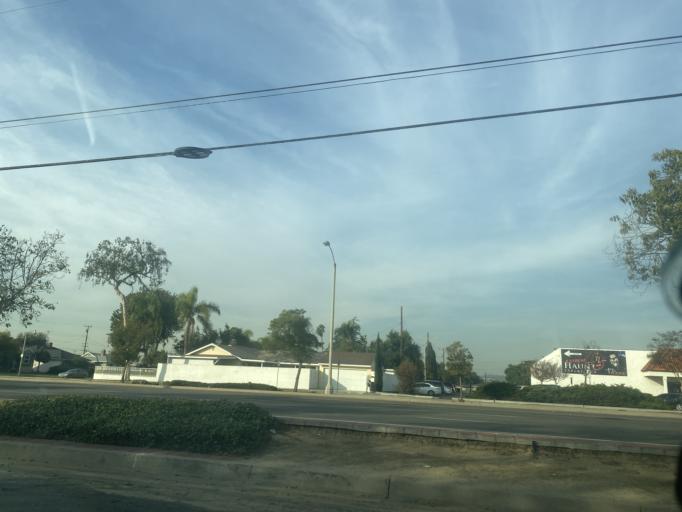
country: US
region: California
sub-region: Orange County
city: Buena Park
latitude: 33.8590
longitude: -117.9622
